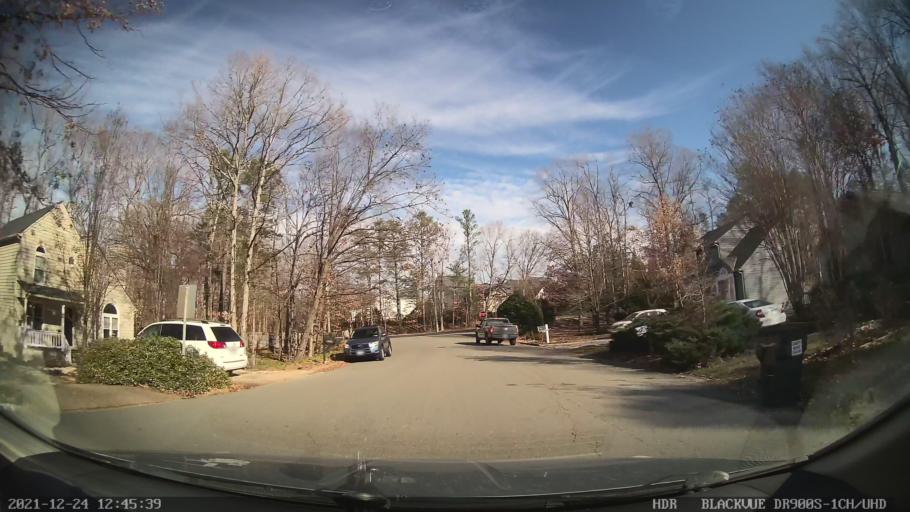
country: US
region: Virginia
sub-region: Henrico County
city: Short Pump
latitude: 37.6325
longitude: -77.6257
